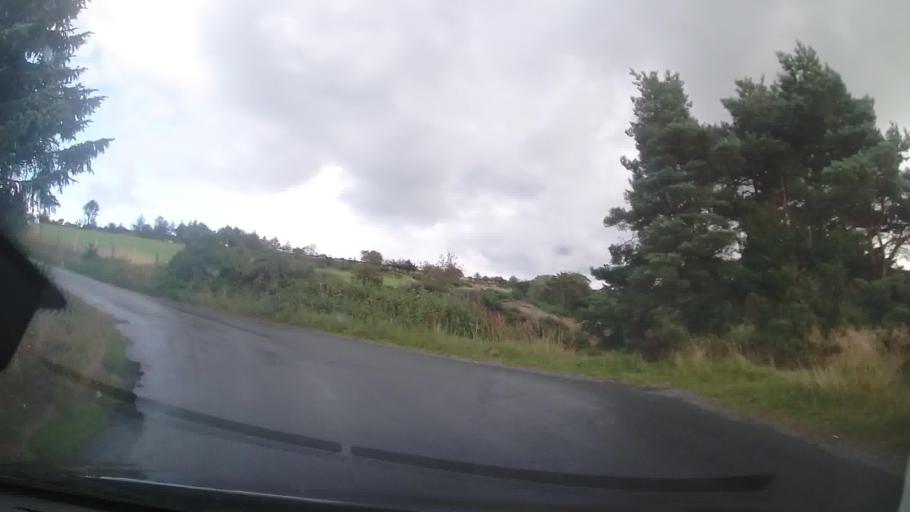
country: GB
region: England
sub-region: Shropshire
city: Norbury
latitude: 52.5746
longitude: -2.9491
